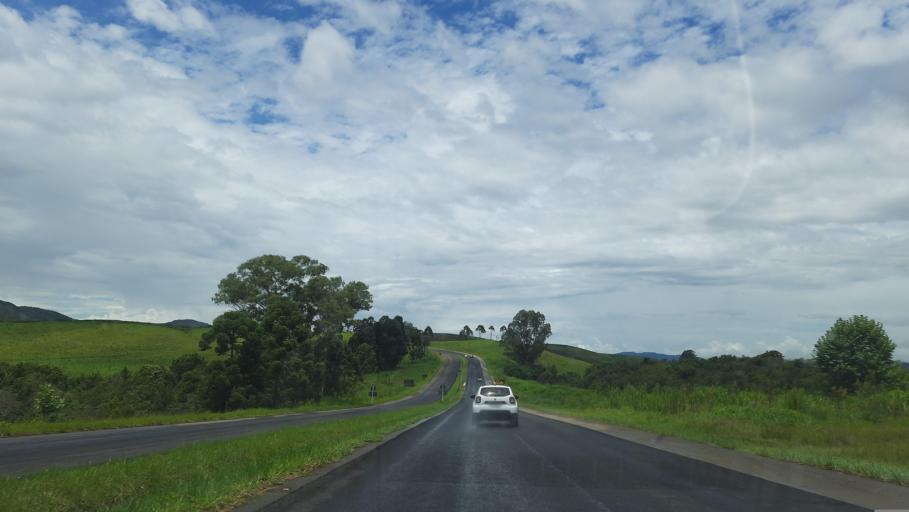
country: BR
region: Minas Gerais
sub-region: Pocos De Caldas
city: Pocos de Caldas
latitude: -21.8371
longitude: -46.6736
